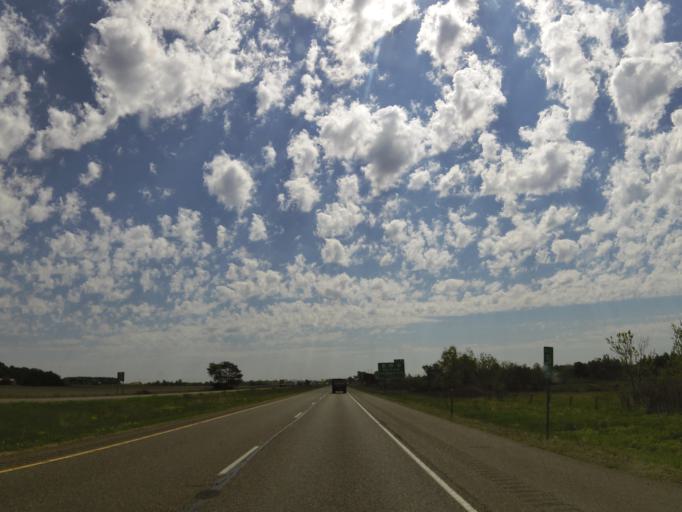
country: US
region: Wisconsin
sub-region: Eau Claire County
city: Eau Claire
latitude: 44.8487
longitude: -91.6272
